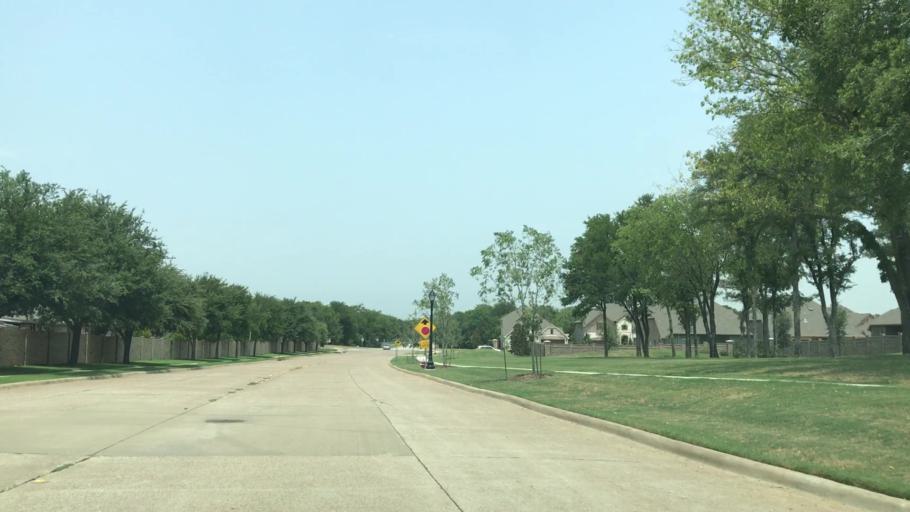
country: US
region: Texas
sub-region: Tarrant County
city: Euless
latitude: 32.8446
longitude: -97.0725
